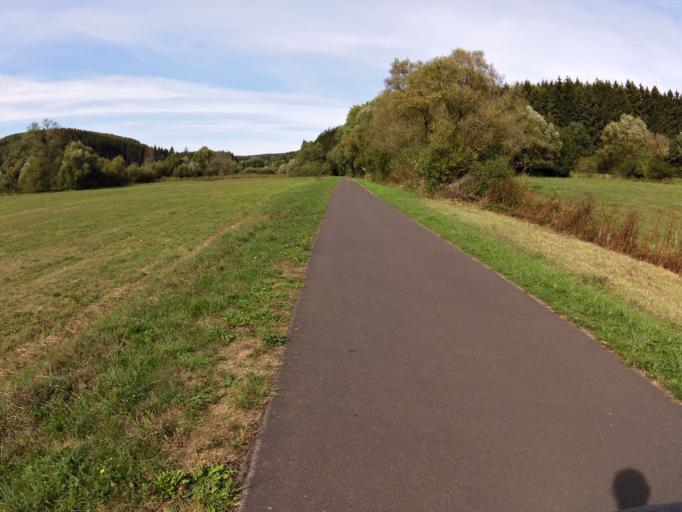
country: DE
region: Rheinland-Pfalz
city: Pronsfeld
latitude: 50.1733
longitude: 6.3169
